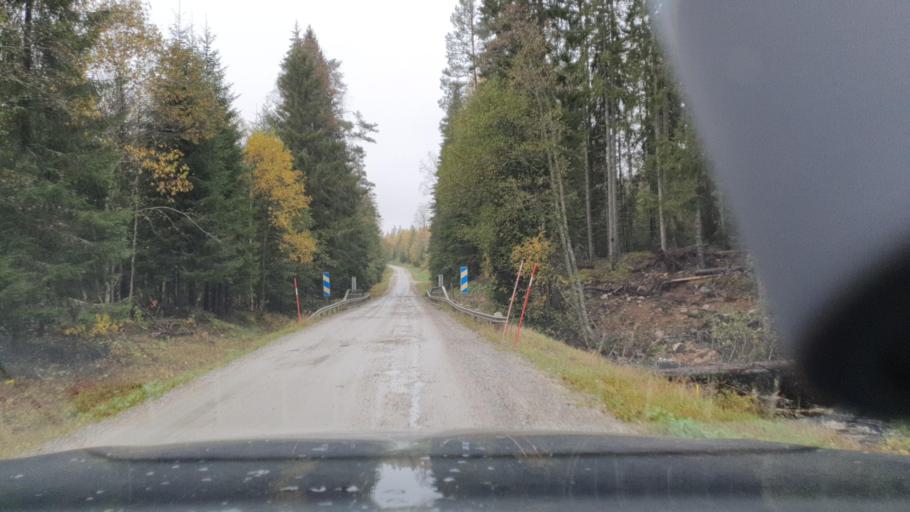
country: SE
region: Vaermland
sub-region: Arvika Kommun
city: Arvika
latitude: 59.8173
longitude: 12.7453
